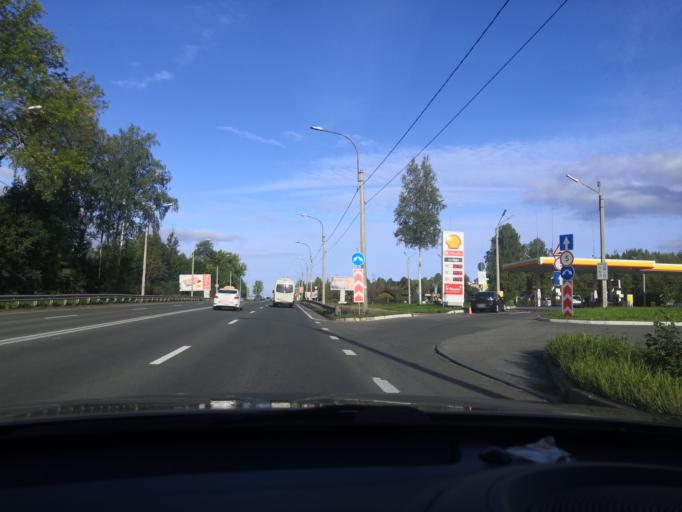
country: RU
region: St.-Petersburg
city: Pargolovo
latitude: 60.0735
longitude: 30.2813
